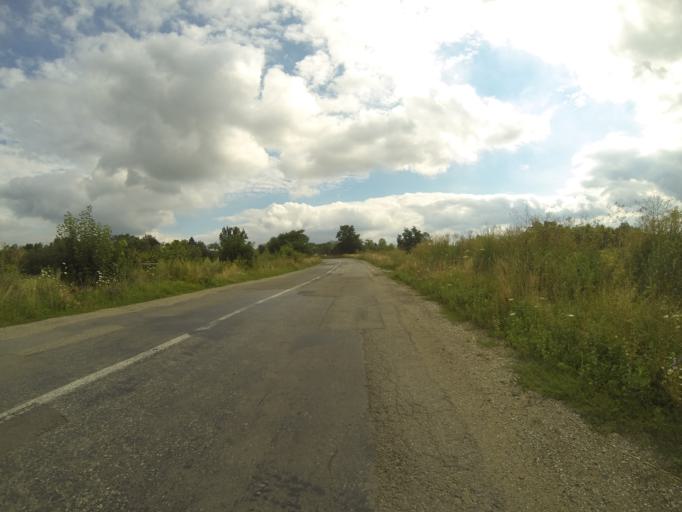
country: RO
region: Brasov
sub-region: Comuna Sinca Veche
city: Sinca Veche
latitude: 45.7883
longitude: 25.1491
